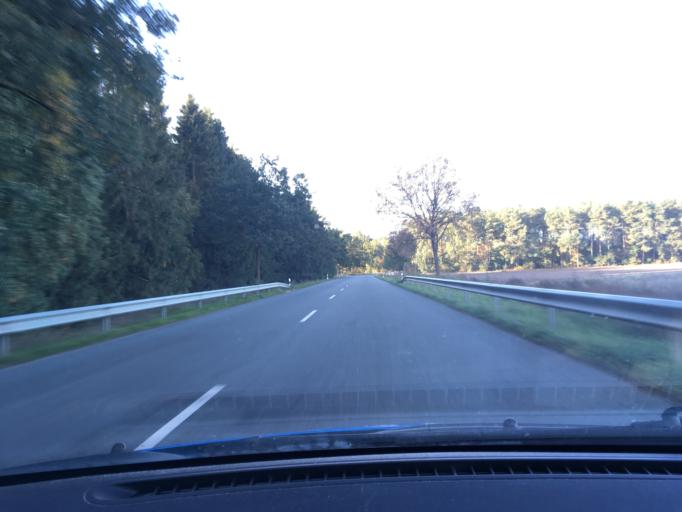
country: DE
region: Lower Saxony
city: Munster
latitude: 53.0096
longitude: 10.0493
